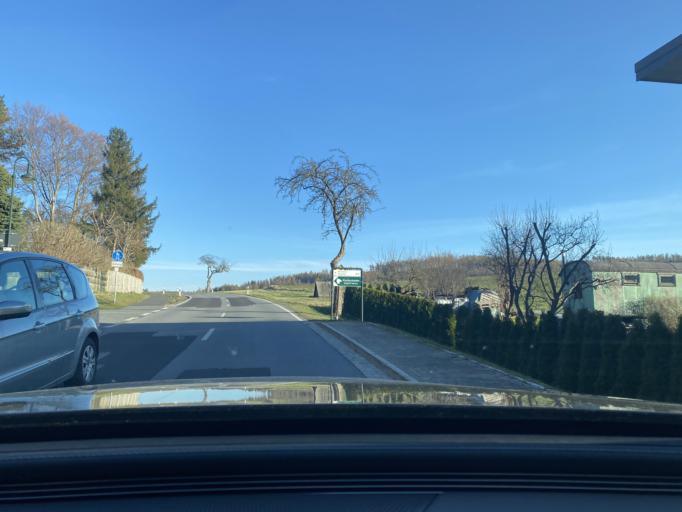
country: DE
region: Saxony
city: Sohland
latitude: 51.0407
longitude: 14.4269
